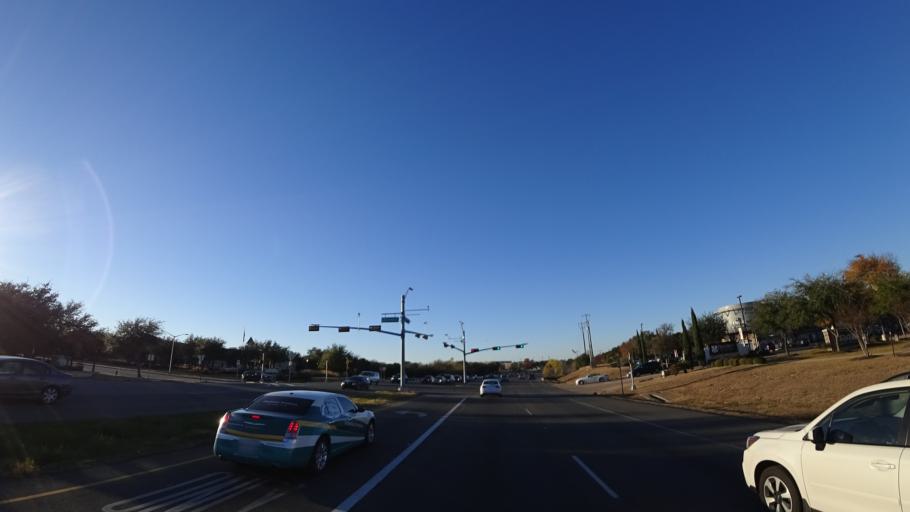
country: US
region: Texas
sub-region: Williamson County
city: Brushy Creek
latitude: 30.5307
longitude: -97.7799
